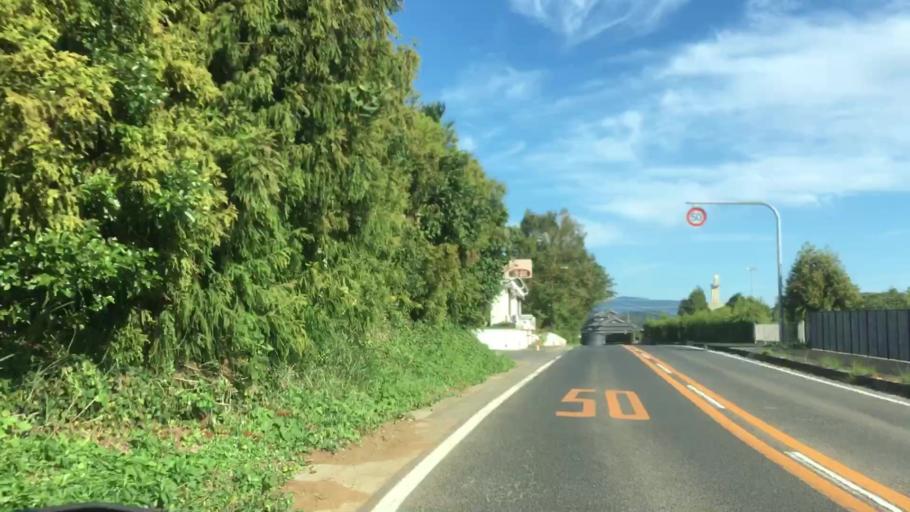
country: JP
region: Nagasaki
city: Sasebo
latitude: 33.0722
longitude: 129.7607
